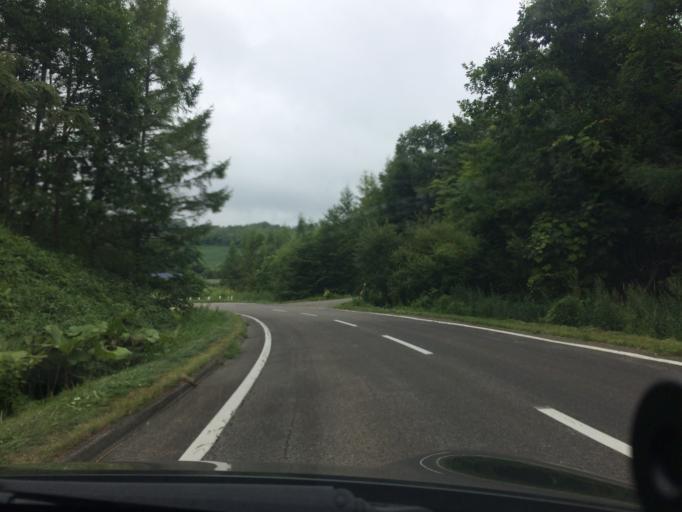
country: JP
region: Hokkaido
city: Otofuke
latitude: 42.9808
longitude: 143.0832
